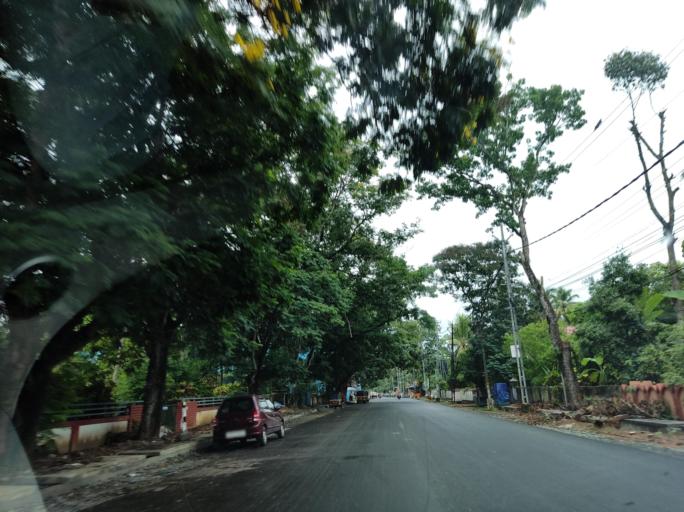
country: IN
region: Kerala
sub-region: Alappuzha
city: Mavelikara
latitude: 9.2507
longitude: 76.5264
